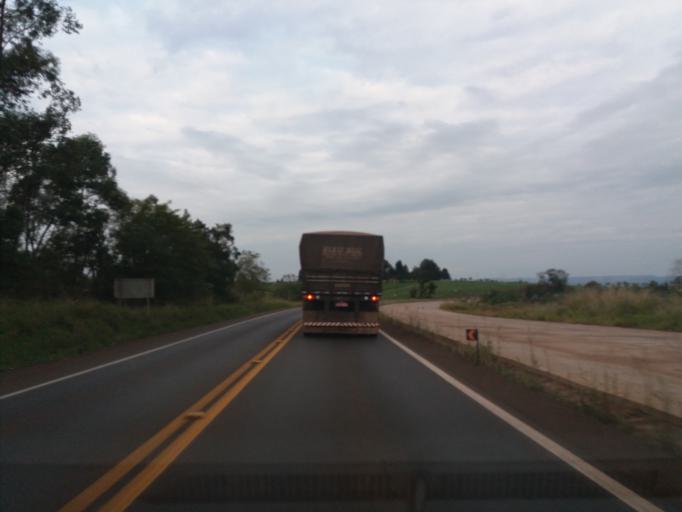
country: BR
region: Parana
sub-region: Cascavel
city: Cascavel
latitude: -25.2421
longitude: -53.5846
